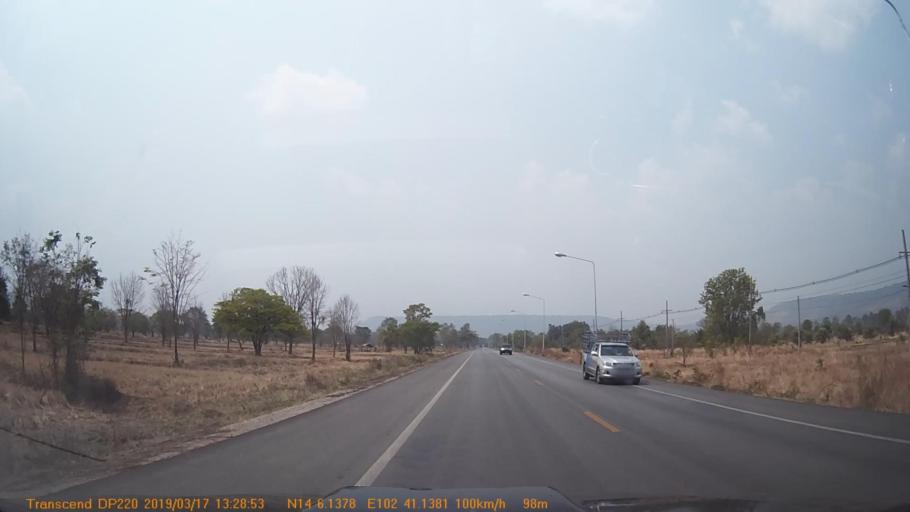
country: TH
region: Sa Kaeo
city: Ta Phraya
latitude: 14.1026
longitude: 102.6853
